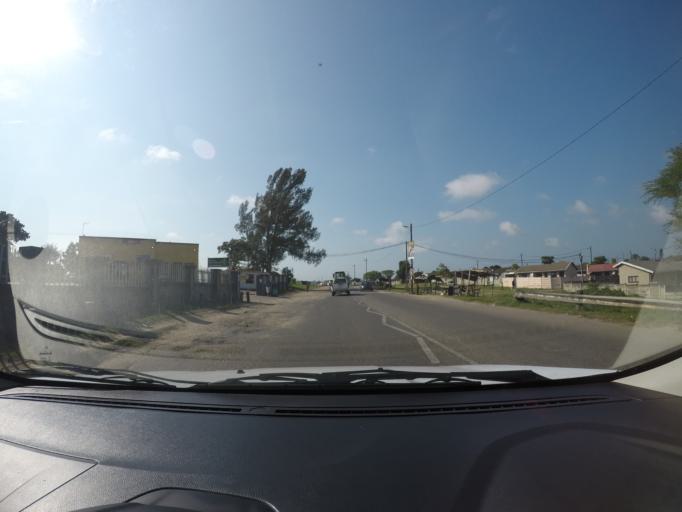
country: ZA
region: KwaZulu-Natal
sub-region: uThungulu District Municipality
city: eSikhawini
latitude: -28.8675
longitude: 31.9265
